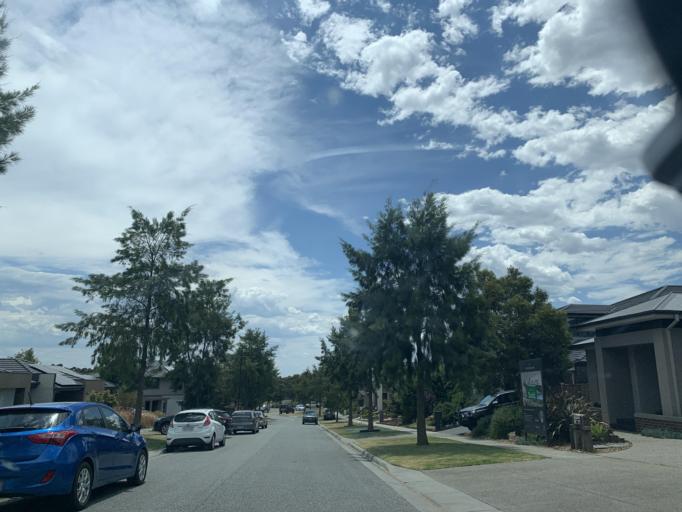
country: AU
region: Victoria
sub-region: Casey
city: Cranbourne South
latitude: -38.1367
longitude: 145.2525
